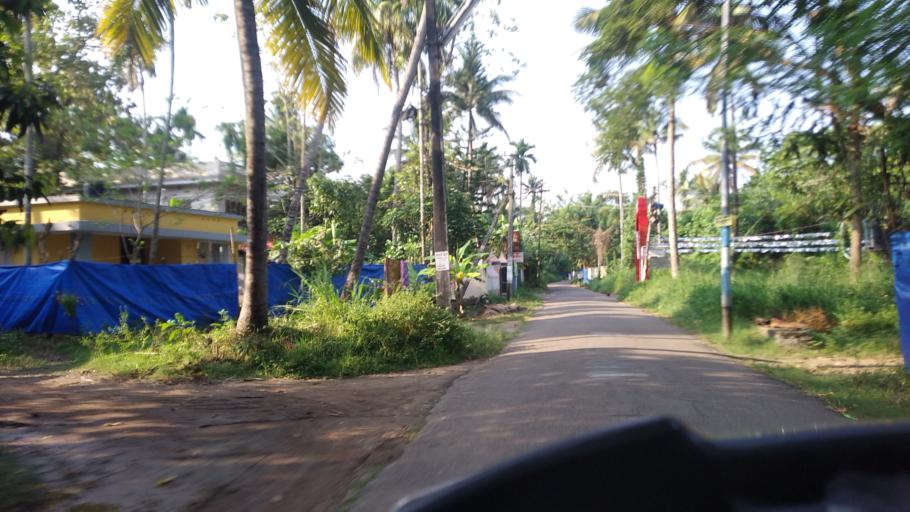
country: IN
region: Kerala
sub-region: Ernakulam
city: Elur
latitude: 10.0422
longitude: 76.2276
